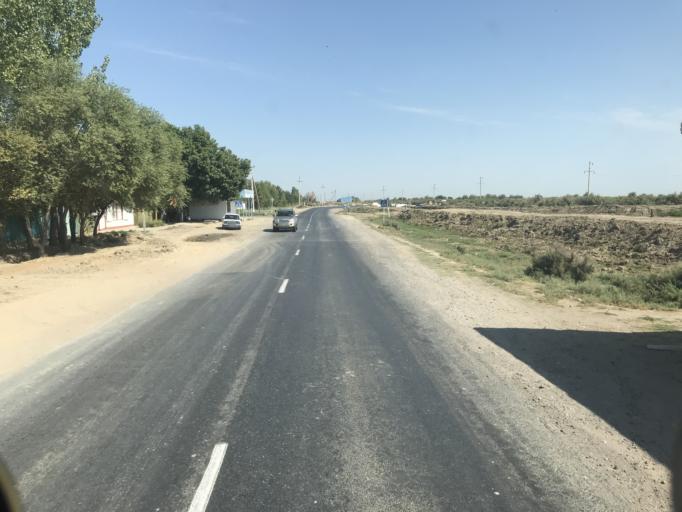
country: KZ
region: Ongtustik Qazaqstan
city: Myrzakent
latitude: 40.7145
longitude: 68.5337
